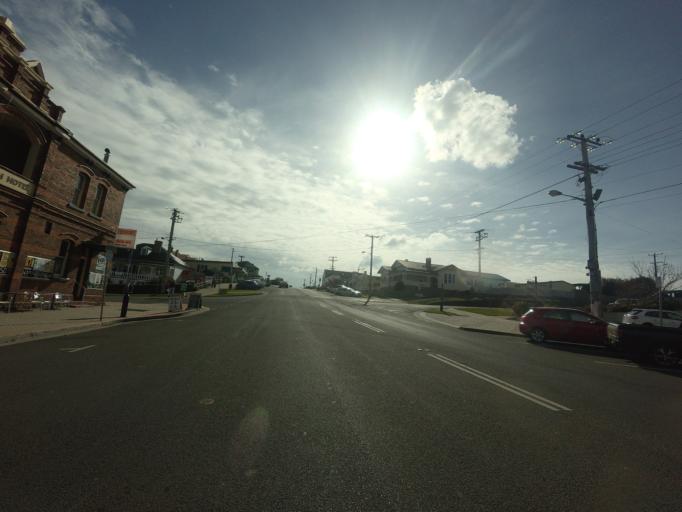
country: AU
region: Tasmania
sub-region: Meander Valley
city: Deloraine
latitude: -41.5243
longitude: 146.6530
